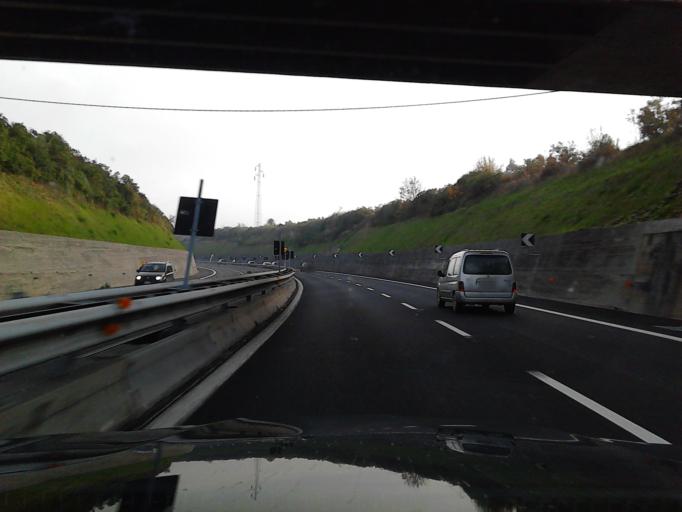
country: IT
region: Abruzzo
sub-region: Provincia di Chieti
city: San Vito Chietino
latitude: 42.3028
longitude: 14.4226
